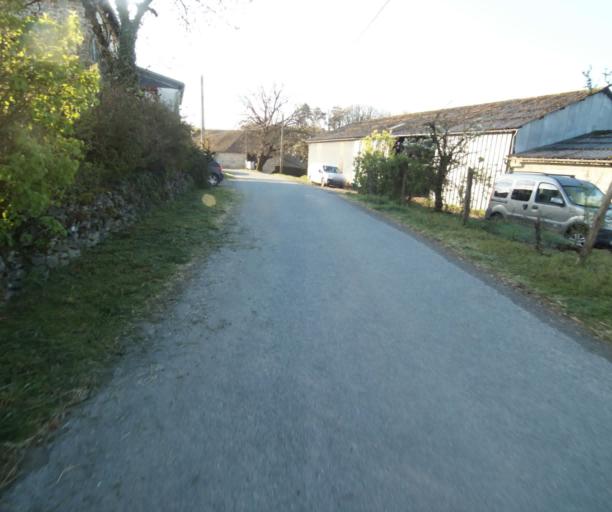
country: FR
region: Limousin
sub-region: Departement de la Correze
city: Correze
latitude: 45.3762
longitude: 1.8551
